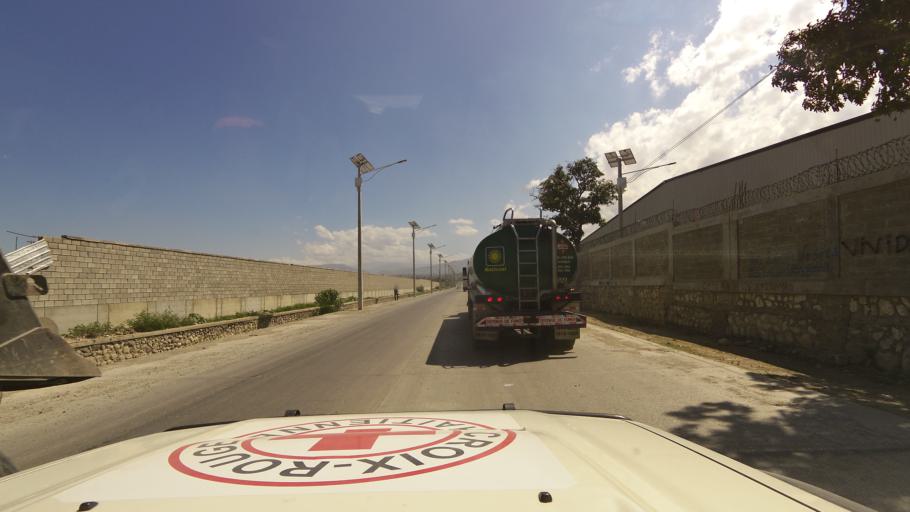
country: HT
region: Ouest
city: Delmas 73
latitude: 18.5880
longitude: -72.3189
